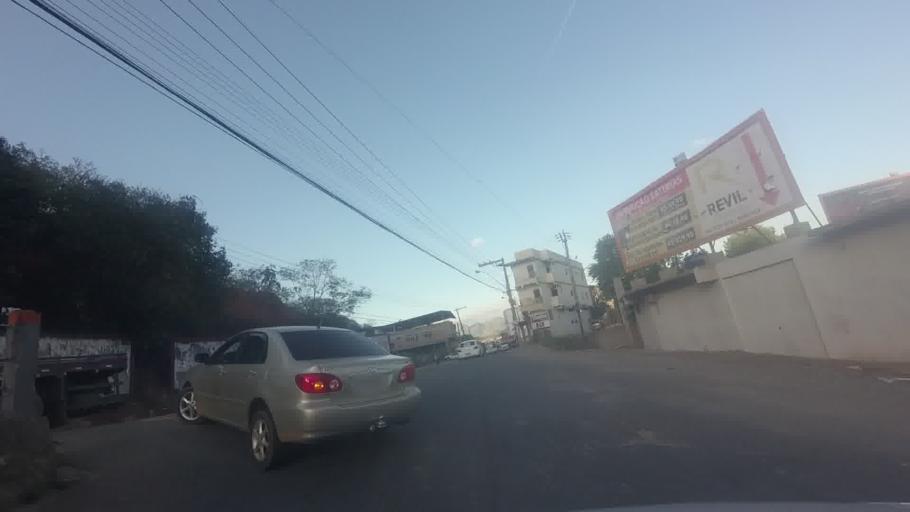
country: BR
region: Espirito Santo
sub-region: Cachoeiro De Itapemirim
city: Cachoeiro de Itapemirim
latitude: -20.8471
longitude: -41.1378
